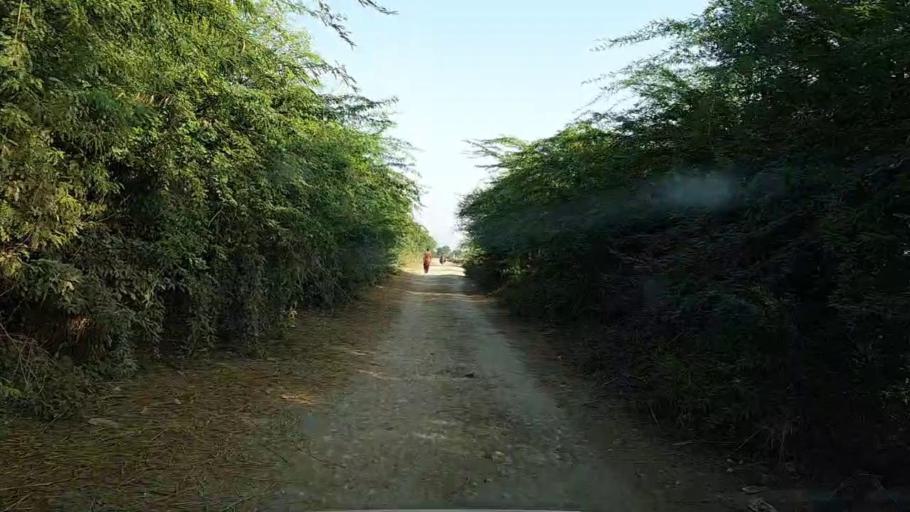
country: PK
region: Sindh
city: Bulri
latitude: 24.7497
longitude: 68.4210
